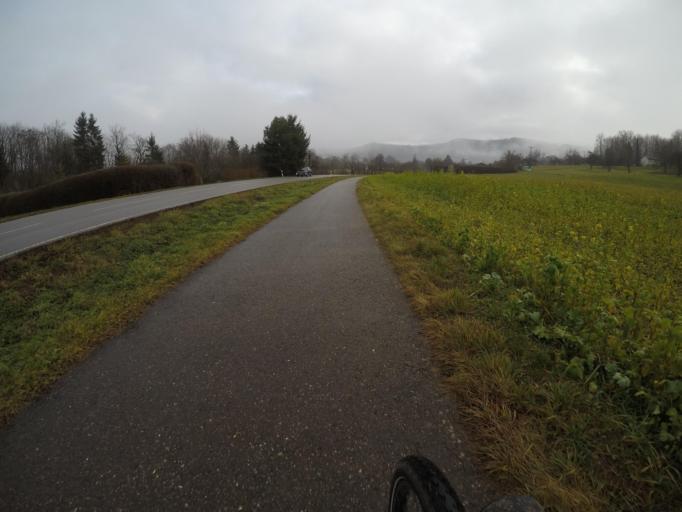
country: DE
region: Baden-Wuerttemberg
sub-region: Regierungsbezirk Stuttgart
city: Beuren
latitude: 48.5767
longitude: 9.3902
